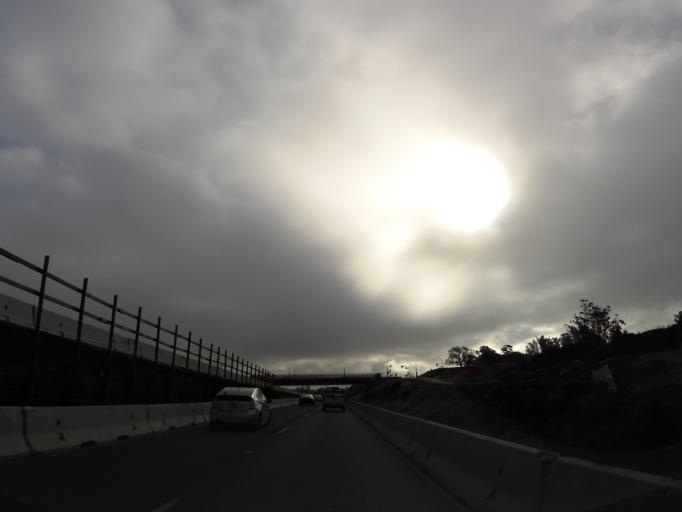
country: US
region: California
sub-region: Sonoma County
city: Petaluma
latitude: 38.2221
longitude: -122.6101
